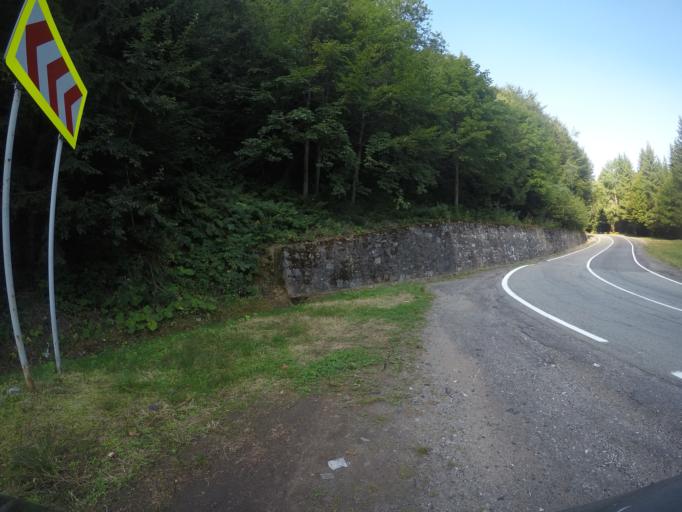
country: RO
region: Sibiu
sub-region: Comuna Cartisoara
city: Cartisoara
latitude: 45.6639
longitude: 24.5946
